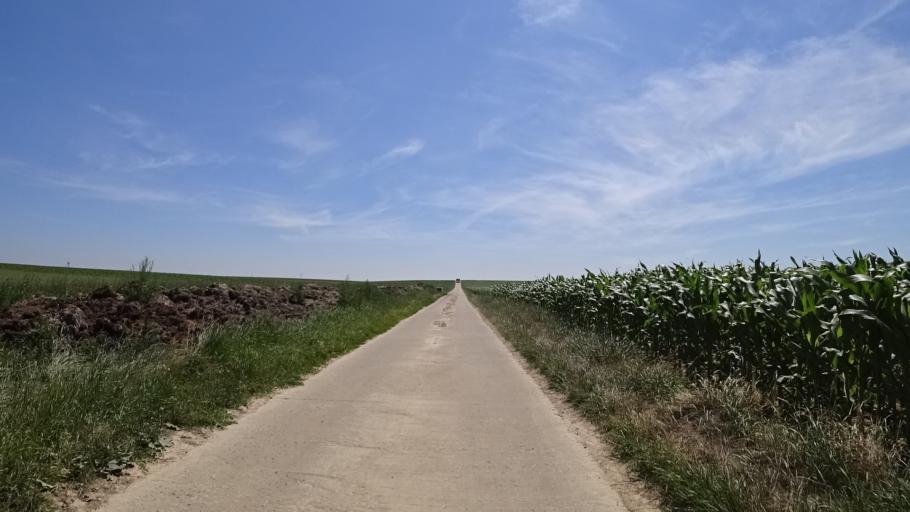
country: BE
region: Wallonia
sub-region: Province du Brabant Wallon
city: Chastre-Villeroux-Blanmont
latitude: 50.6032
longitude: 4.6632
